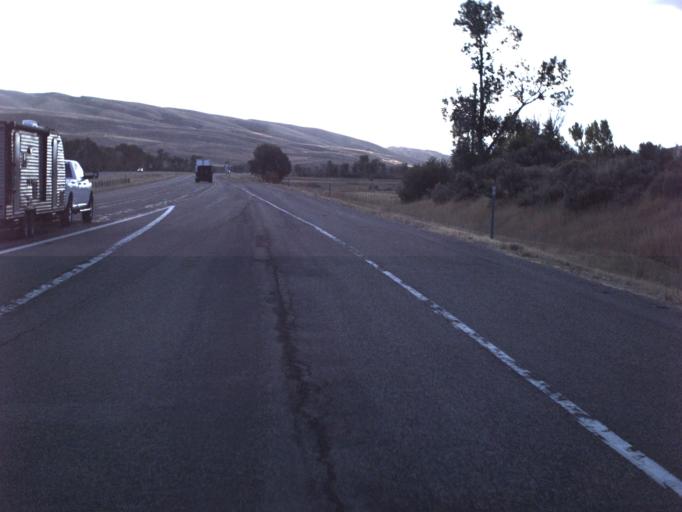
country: US
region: Utah
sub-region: Morgan County
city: Morgan
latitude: 41.0419
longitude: -111.5203
